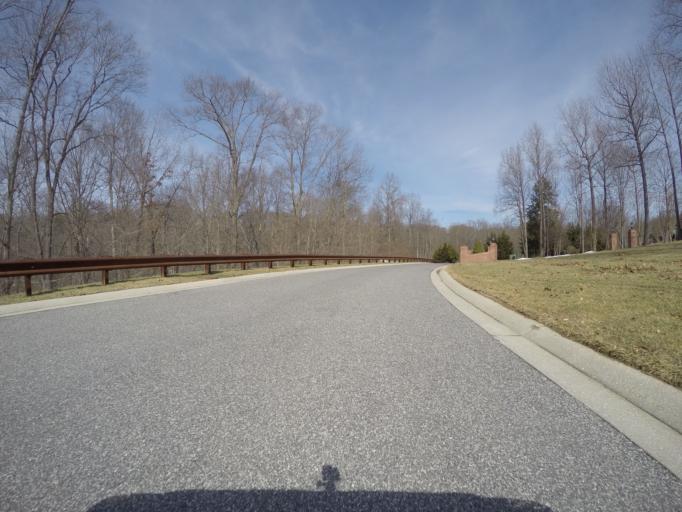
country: US
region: Maryland
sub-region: Baltimore County
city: Hunt Valley
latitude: 39.5100
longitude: -76.6557
